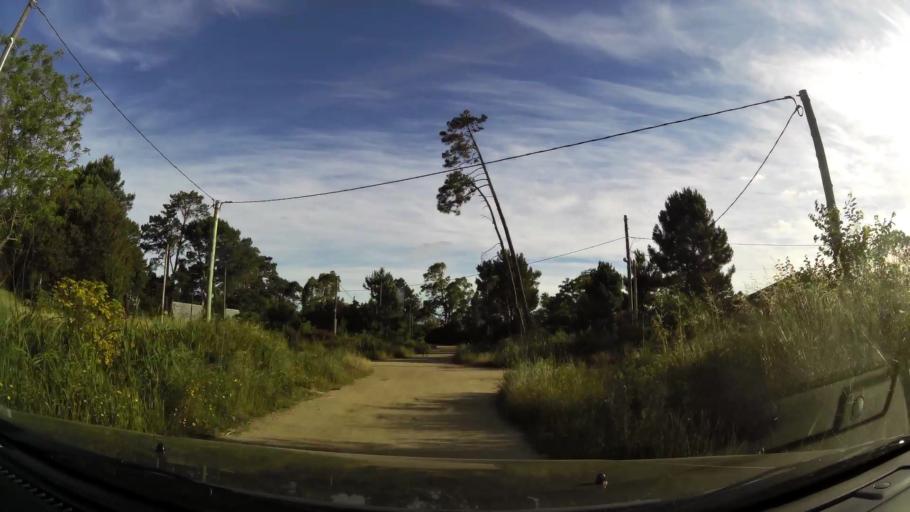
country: UY
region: Canelones
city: Empalme Olmos
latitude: -34.7712
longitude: -55.8597
